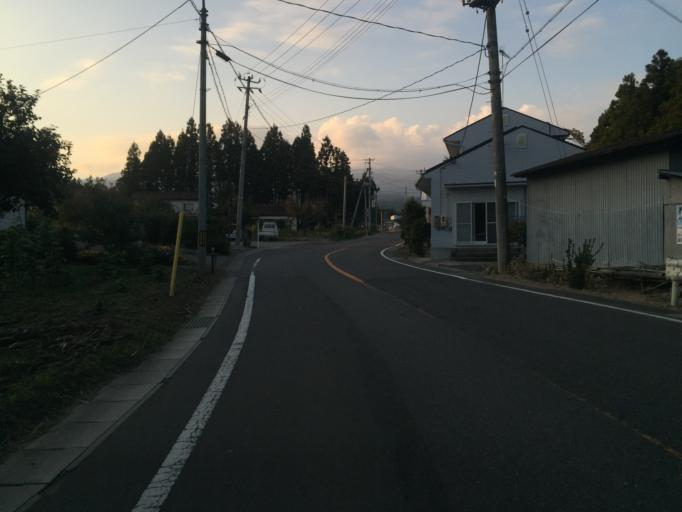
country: JP
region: Fukushima
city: Motomiya
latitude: 37.5545
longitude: 140.3577
